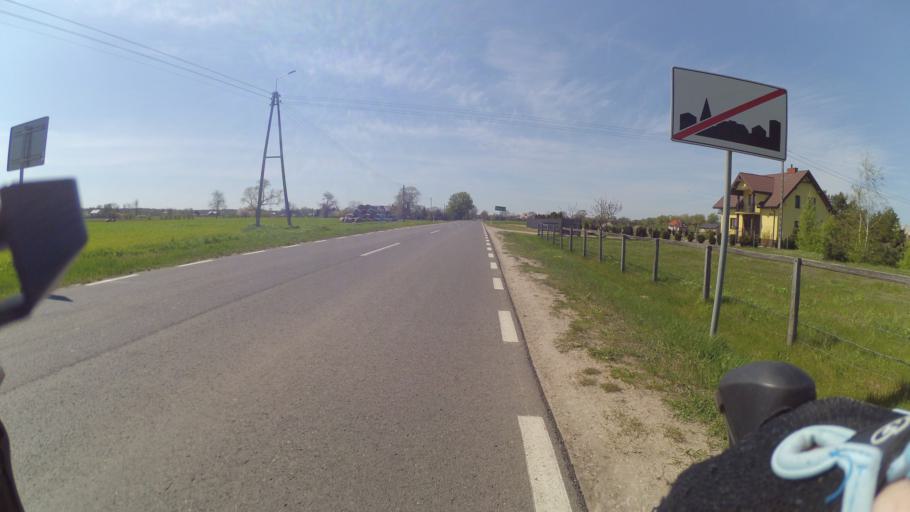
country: PL
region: Masovian Voivodeship
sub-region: Powiat plonski
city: Czerwinsk Nad Wisla
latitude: 52.3781
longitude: 20.3322
